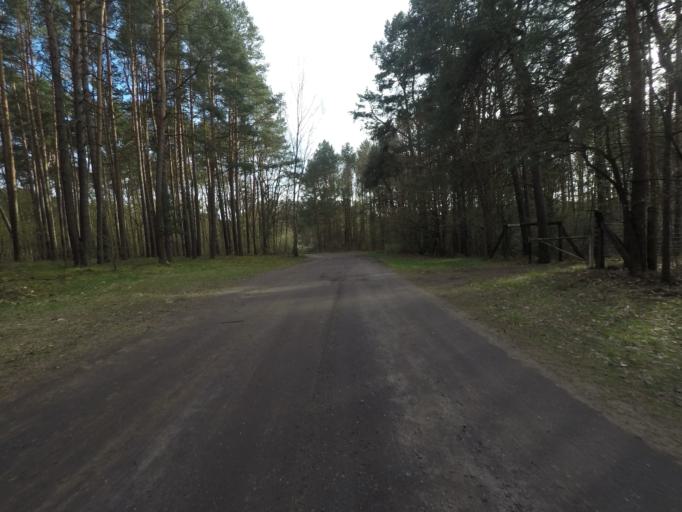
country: DE
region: Brandenburg
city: Marienwerder
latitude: 52.8525
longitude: 13.6536
